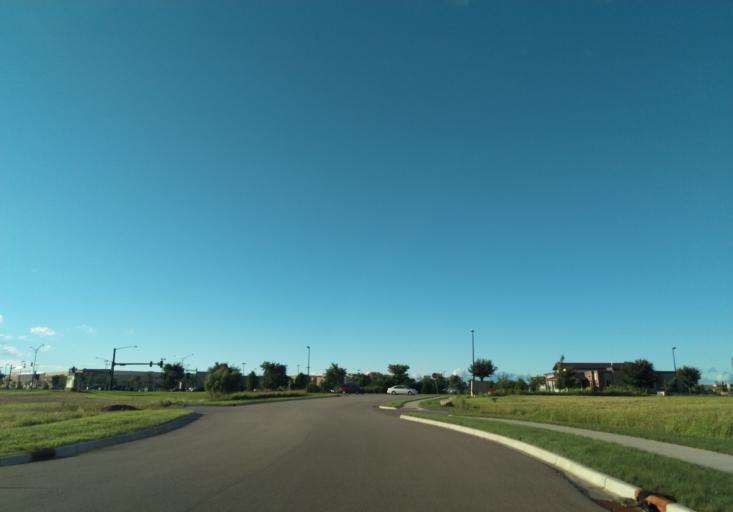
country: US
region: Wisconsin
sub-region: Dane County
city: Sun Prairie
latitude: 43.1650
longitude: -89.2715
